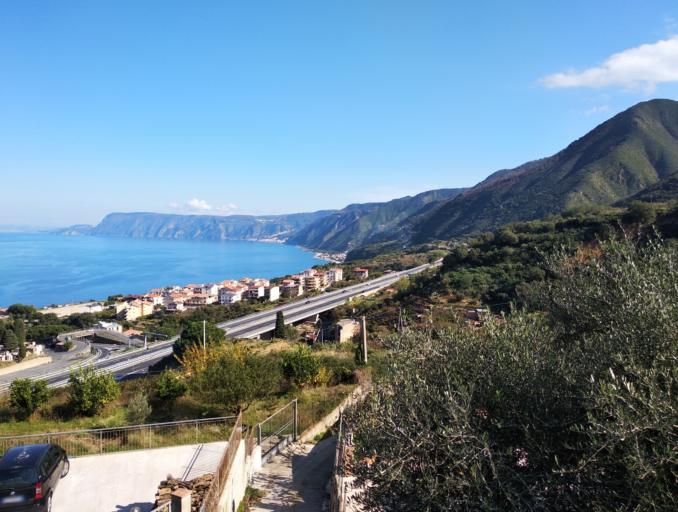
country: IT
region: Calabria
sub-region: Provincia di Reggio Calabria
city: Scilla
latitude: 38.2470
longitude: 15.7192
